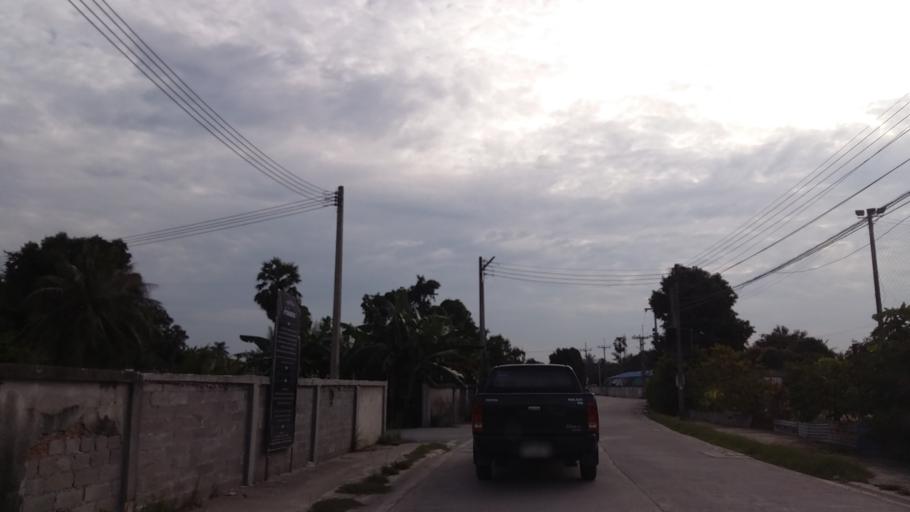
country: TH
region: Chon Buri
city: Chon Buri
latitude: 13.3028
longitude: 100.9396
